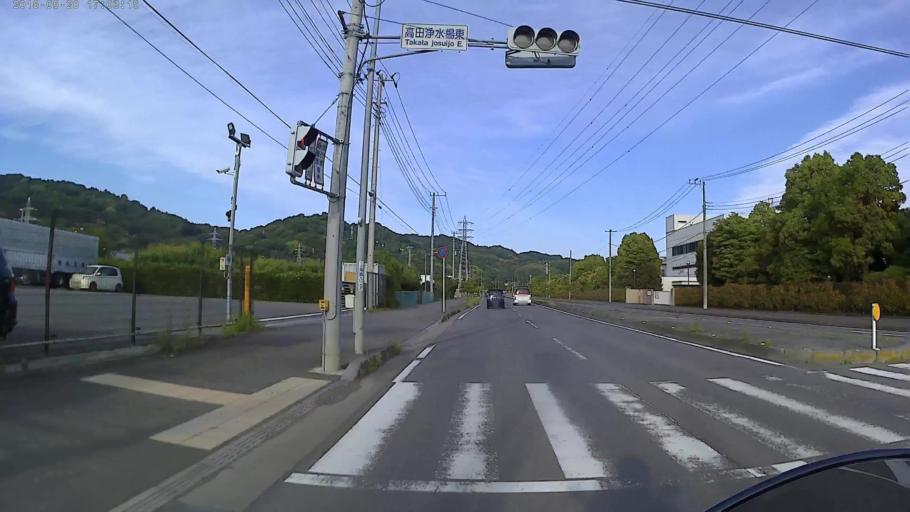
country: JP
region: Kanagawa
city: Odawara
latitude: 35.2895
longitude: 139.1929
